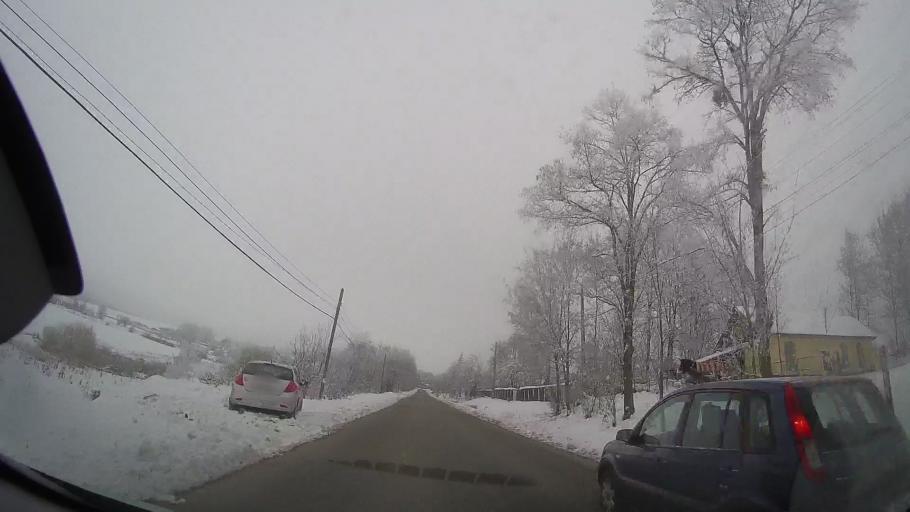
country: RO
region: Neamt
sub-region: Comuna Icusesti
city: Balusesti
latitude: 46.8587
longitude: 27.0225
